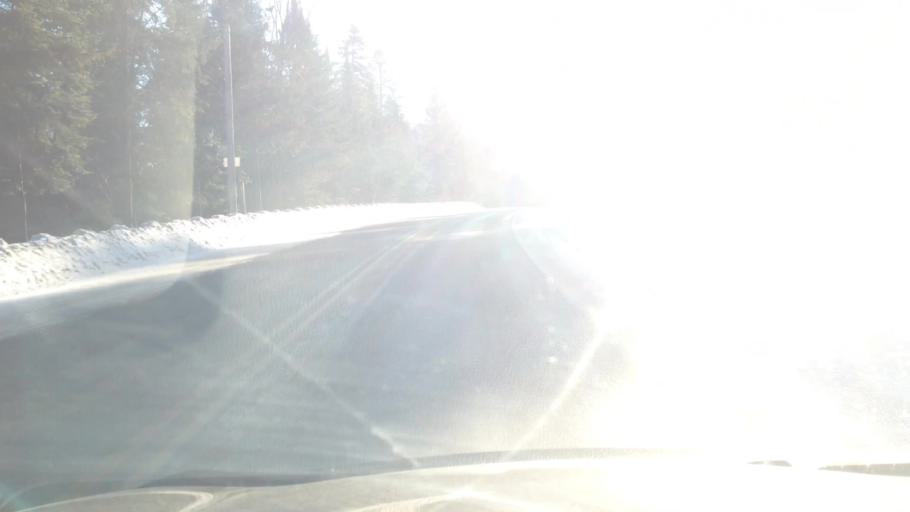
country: CA
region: Quebec
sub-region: Laurentides
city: Sainte-Agathe-des-Monts
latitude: 45.9176
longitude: -74.3747
